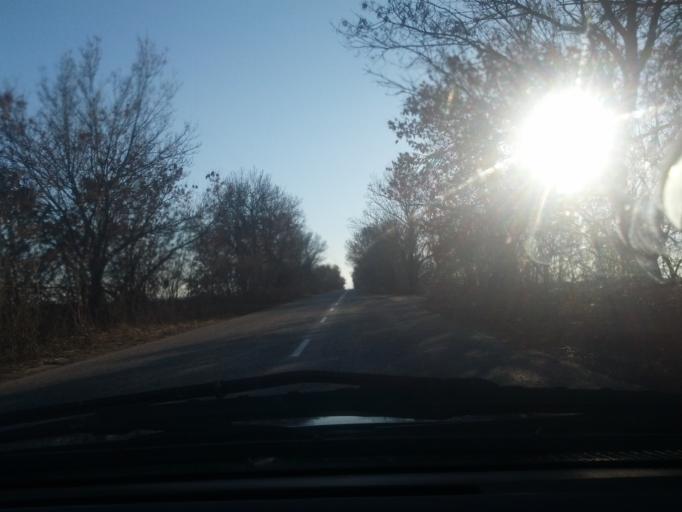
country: BG
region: Vratsa
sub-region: Obshtina Miziya
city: Miziya
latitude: 43.5676
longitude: 23.8098
